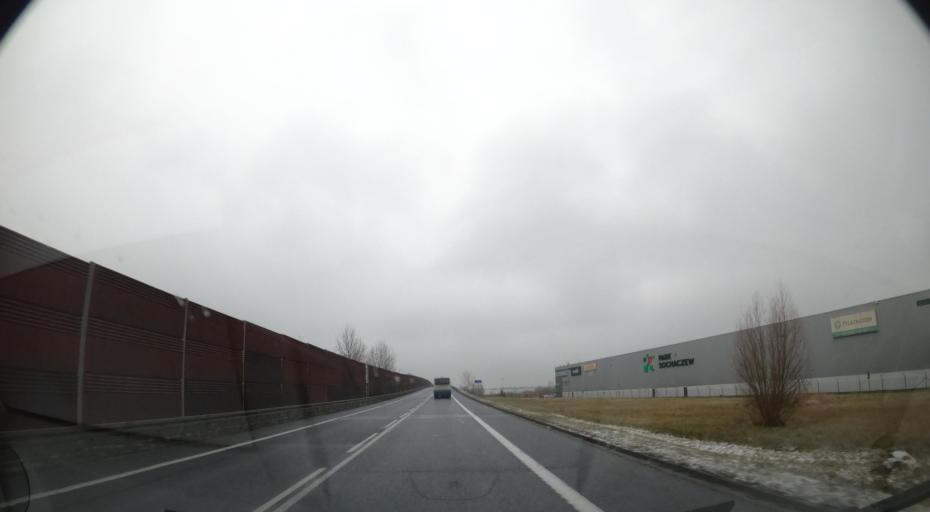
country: PL
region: Masovian Voivodeship
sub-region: Powiat sochaczewski
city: Sochaczew
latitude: 52.2219
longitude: 20.2596
